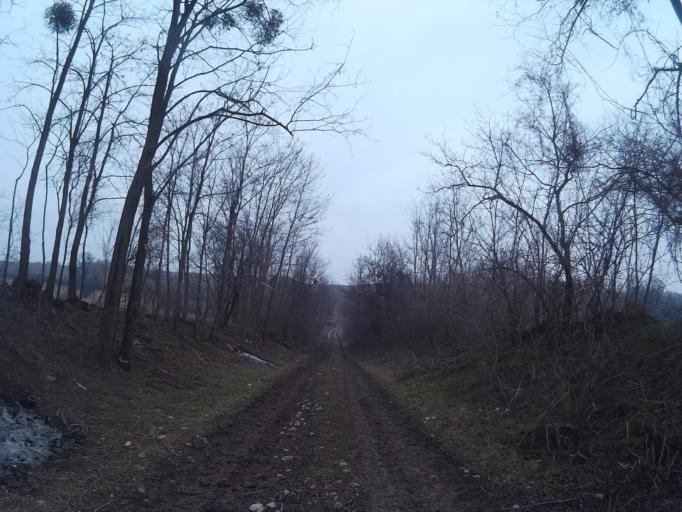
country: HU
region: Fejer
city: Szarliget
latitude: 47.5478
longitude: 18.5699
